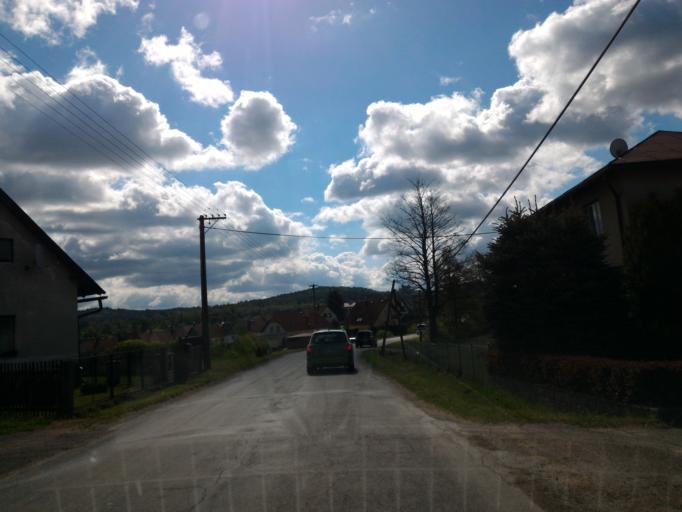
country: CZ
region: Vysocina
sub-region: Okres Havlickuv Brod
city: Svetla nad Sazavou
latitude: 49.6302
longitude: 15.3772
